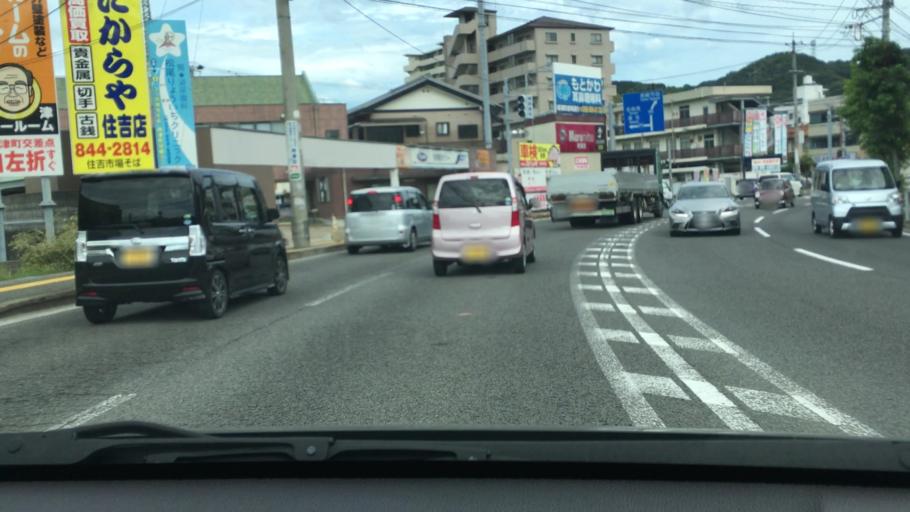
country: JP
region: Nagasaki
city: Togitsu
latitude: 32.8315
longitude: 129.8469
